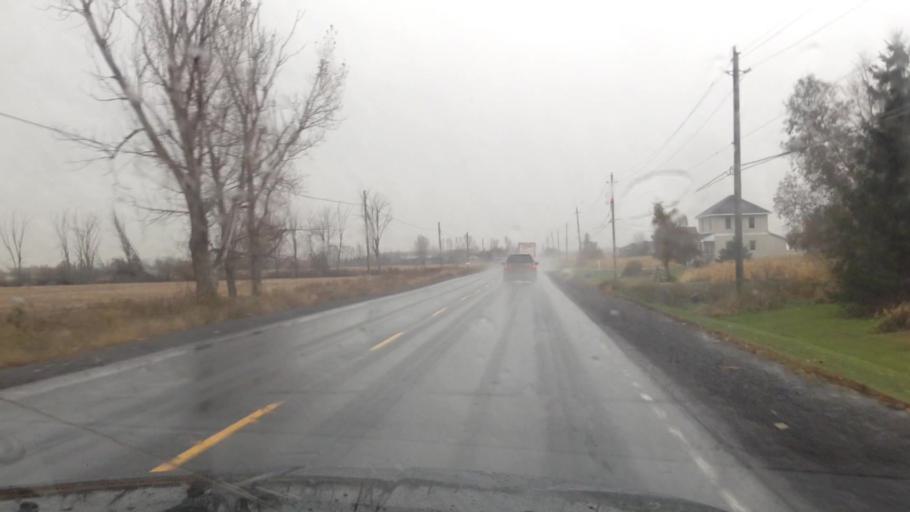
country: CA
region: Ontario
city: Bourget
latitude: 45.2912
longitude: -75.3231
